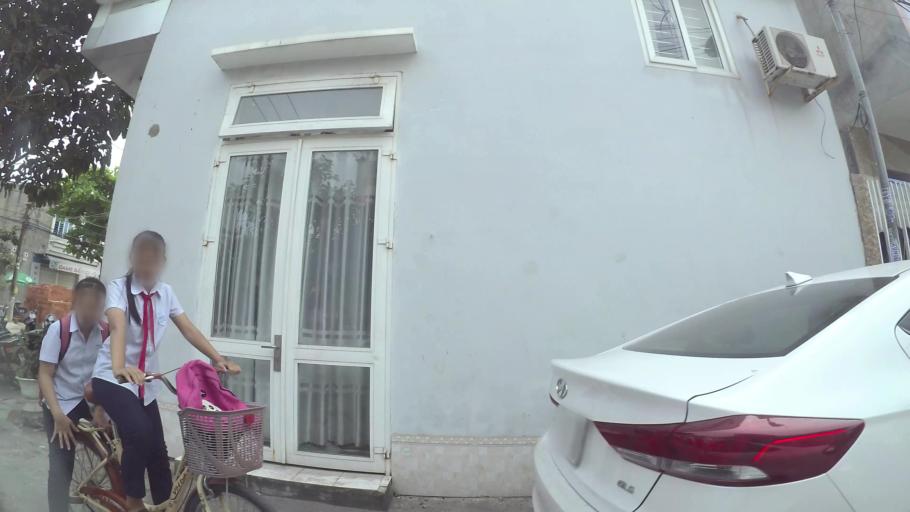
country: VN
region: Da Nang
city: Son Tra
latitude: 16.0938
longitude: 108.2461
